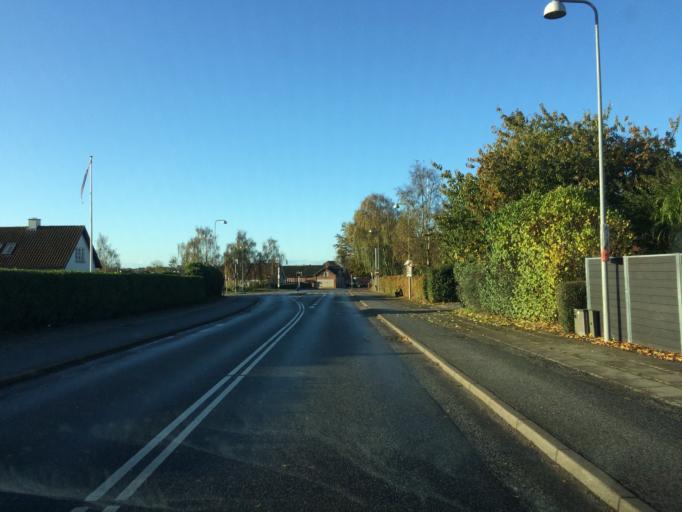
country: DK
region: South Denmark
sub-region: Kolding Kommune
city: Kolding
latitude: 55.5149
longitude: 9.5353
